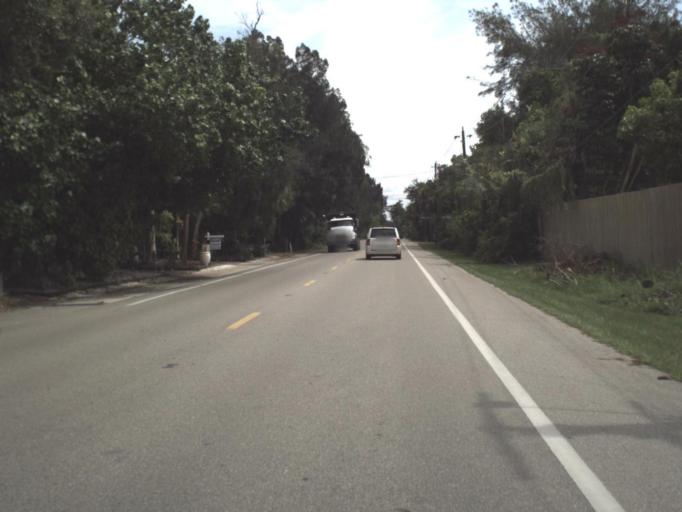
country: US
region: Florida
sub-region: Sarasota County
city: South Sarasota
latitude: 27.2799
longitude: -82.5514
